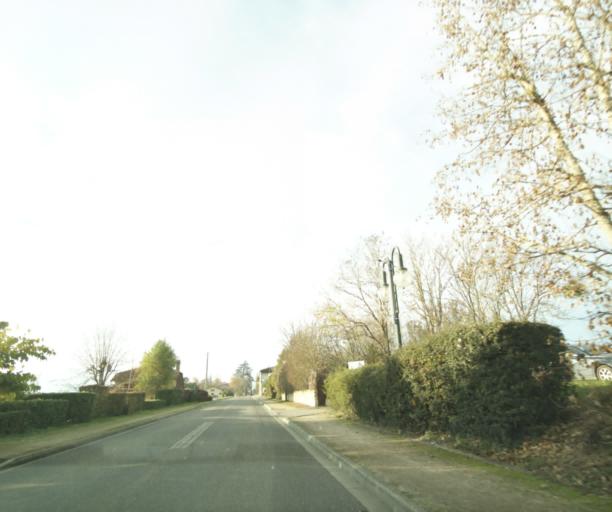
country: FR
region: Midi-Pyrenees
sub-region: Departement du Gers
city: Cazaubon
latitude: 43.9334
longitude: -0.0569
